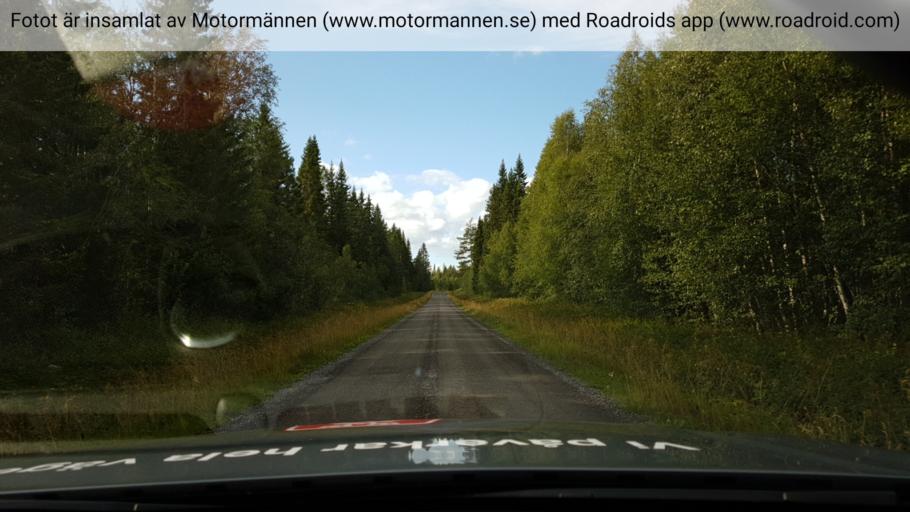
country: SE
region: Jaemtland
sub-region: OEstersunds Kommun
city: Lit
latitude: 63.3091
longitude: 15.2453
